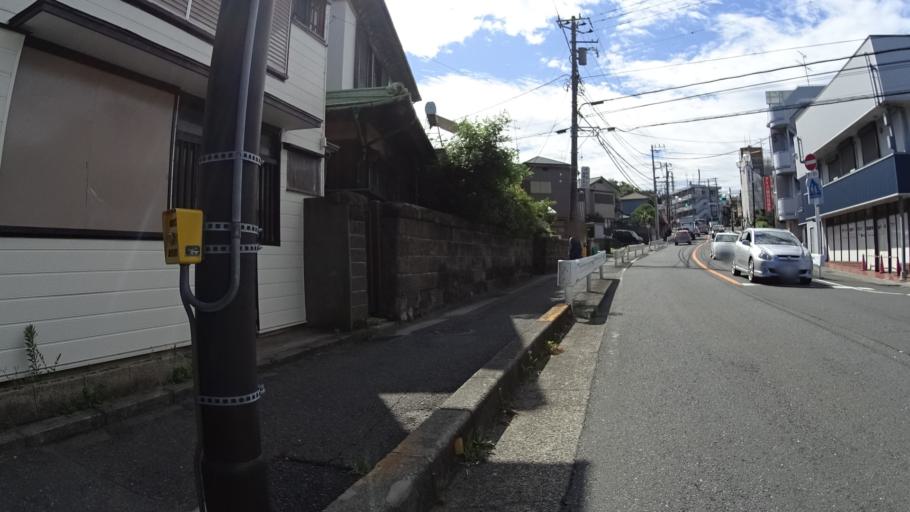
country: JP
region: Kanagawa
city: Yokosuka
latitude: 35.2597
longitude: 139.7054
